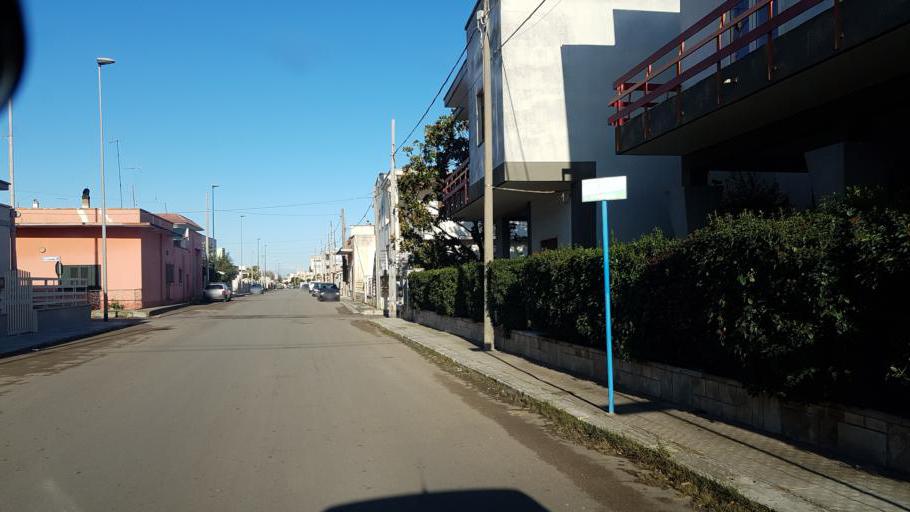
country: IT
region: Apulia
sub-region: Provincia di Brindisi
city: Torchiarolo
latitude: 40.4822
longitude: 18.0504
